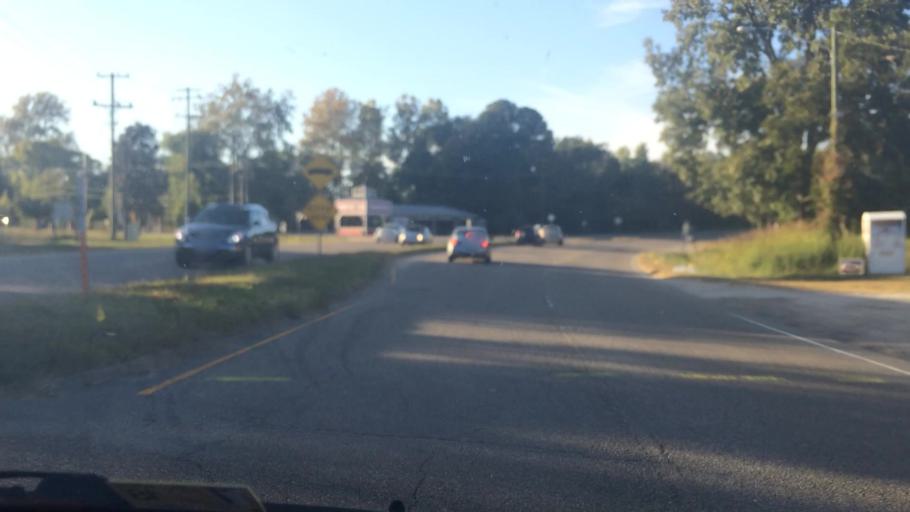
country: US
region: Virginia
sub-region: James City County
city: Williamsburg
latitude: 37.3766
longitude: -76.7875
